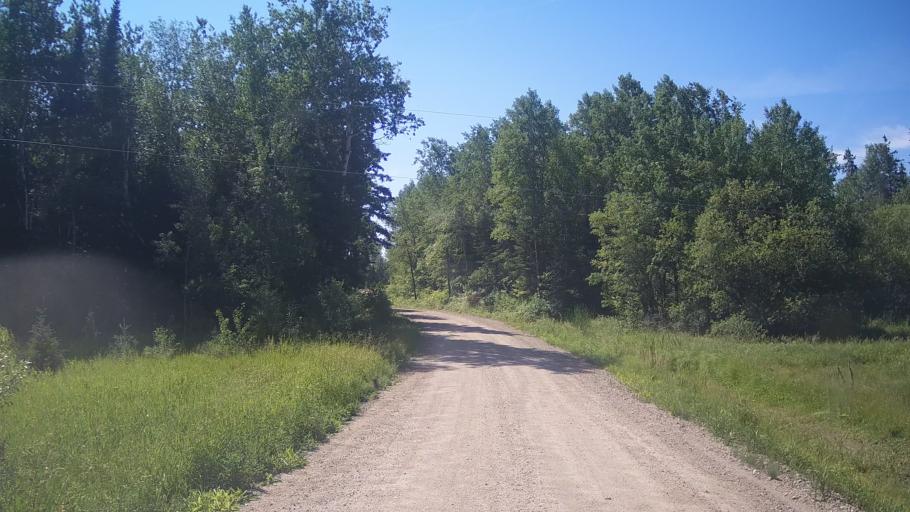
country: CA
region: Ontario
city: Dryden
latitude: 49.8217
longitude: -93.3387
